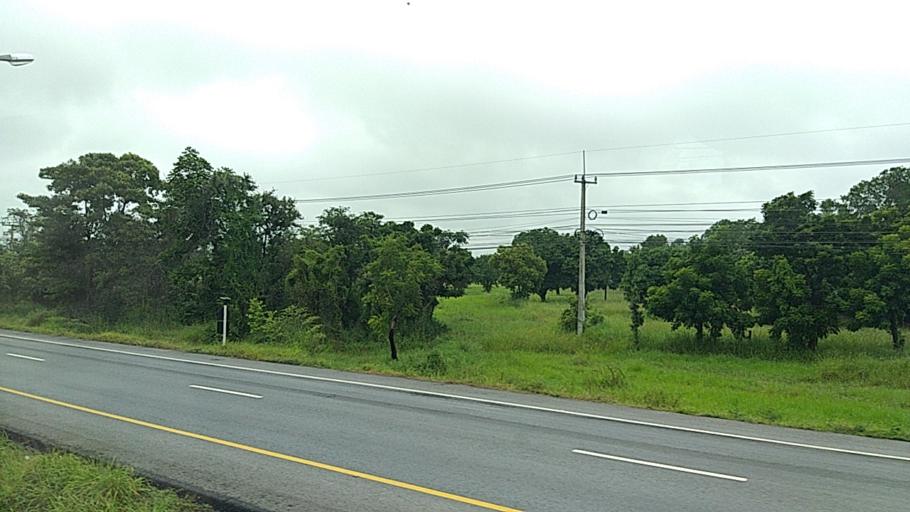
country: TH
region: Nakhon Ratchasima
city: Non Daeng
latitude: 15.3549
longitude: 102.4493
